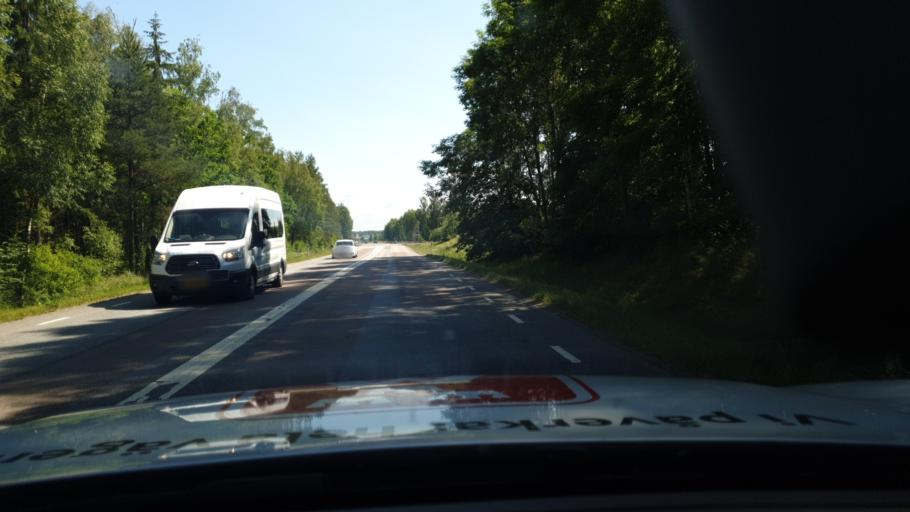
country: SE
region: Vaestra Goetaland
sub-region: Lidkopings Kommun
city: Lidkoping
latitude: 58.5125
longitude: 13.1169
